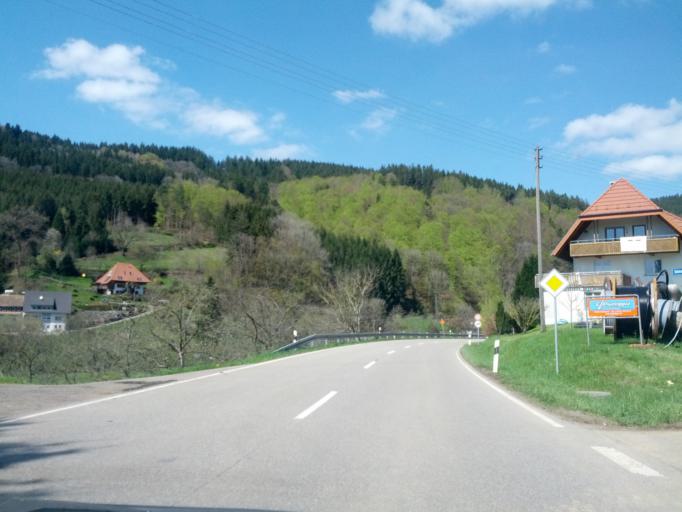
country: DE
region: Baden-Wuerttemberg
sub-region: Freiburg Region
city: Elzach
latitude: 48.1940
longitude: 8.0996
